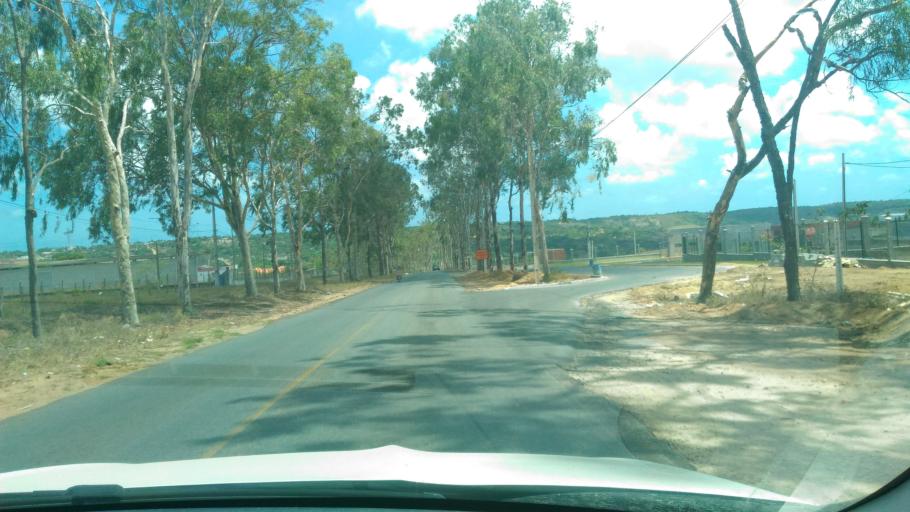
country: BR
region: Paraiba
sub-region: Conde
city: Conde
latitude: -7.2612
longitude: -34.9324
